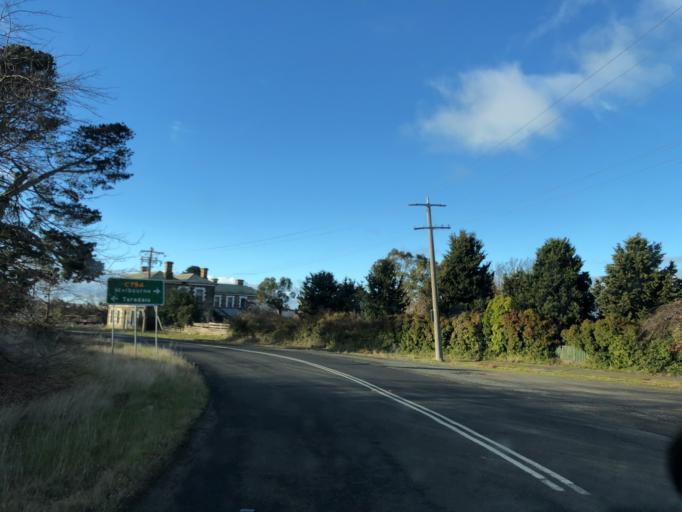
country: AU
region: Victoria
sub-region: Mount Alexander
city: Castlemaine
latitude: -37.1887
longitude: 144.3751
